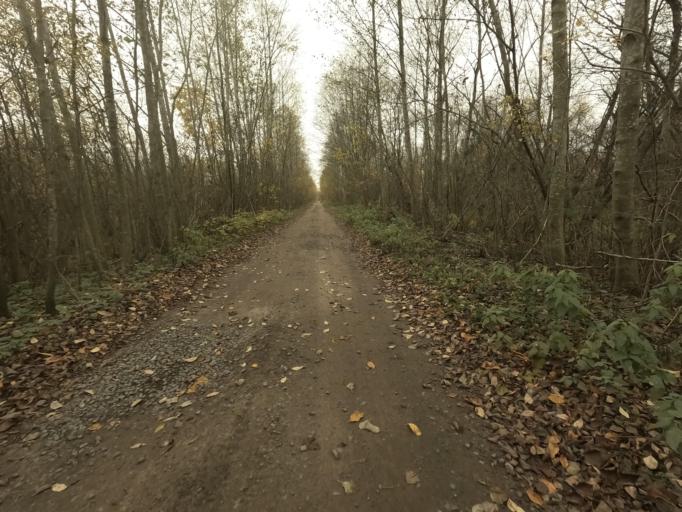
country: RU
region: Leningrad
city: Pavlovo
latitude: 59.7878
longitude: 30.8863
